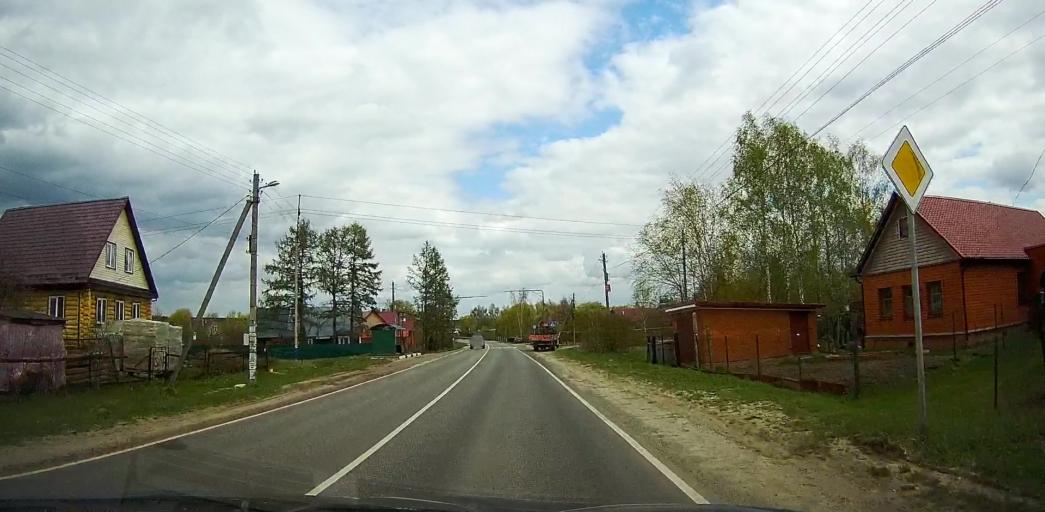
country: RU
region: Moskovskaya
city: Ashitkovo
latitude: 55.4607
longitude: 38.6014
